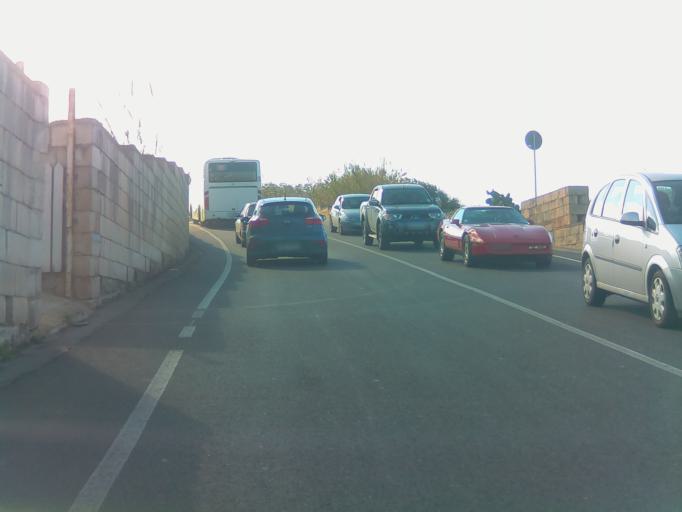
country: MT
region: L-Imgarr
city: Imgarr
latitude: 35.9303
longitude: 14.3503
